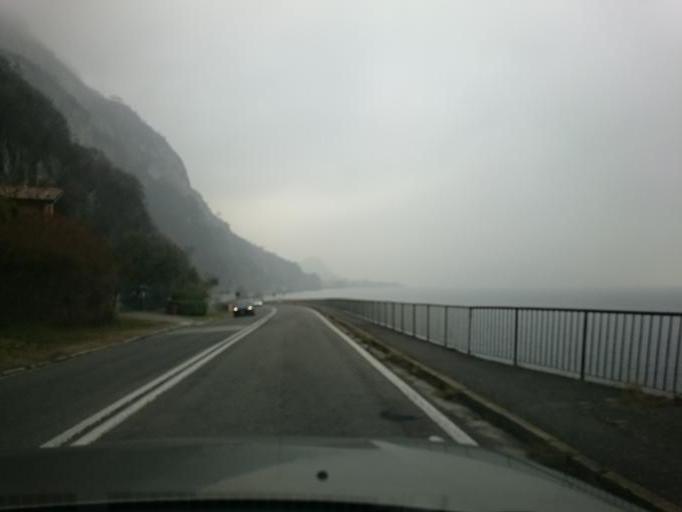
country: IT
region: Lombardy
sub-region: Provincia di Brescia
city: Marone
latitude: 45.7520
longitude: 10.0846
